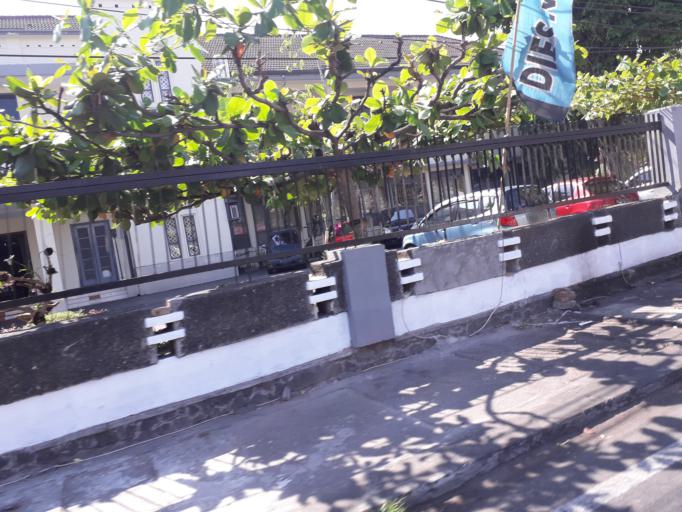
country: ID
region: Daerah Istimewa Yogyakarta
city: Yogyakarta
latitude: -7.7744
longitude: 110.3751
